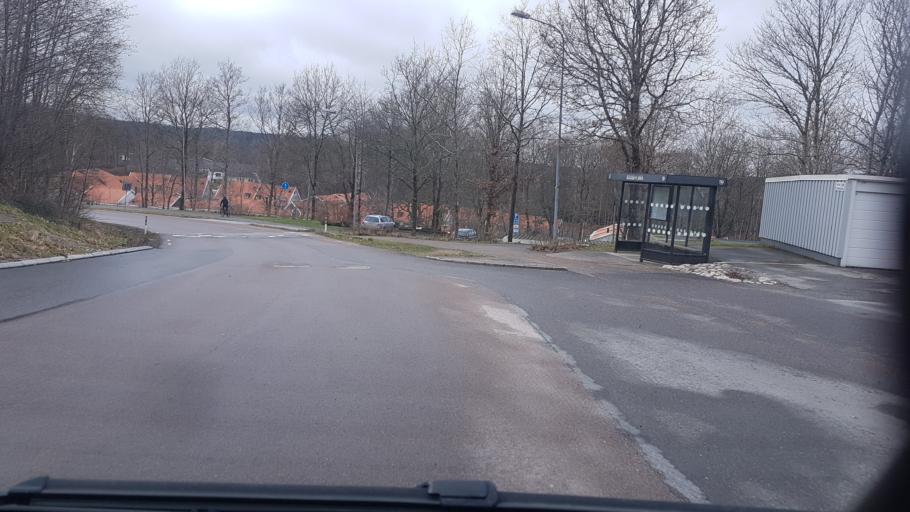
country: SE
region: Vaestra Goetaland
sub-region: Lerums Kommun
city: Lerum
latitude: 57.7546
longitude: 12.2620
